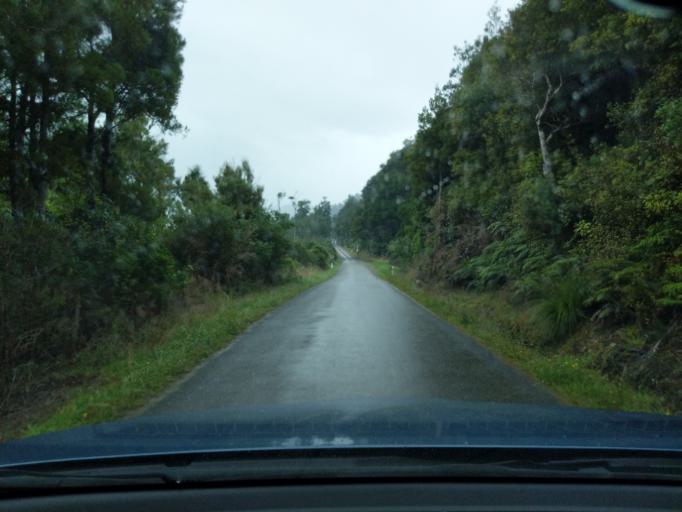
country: NZ
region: Tasman
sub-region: Tasman District
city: Takaka
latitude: -40.6424
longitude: 172.4827
